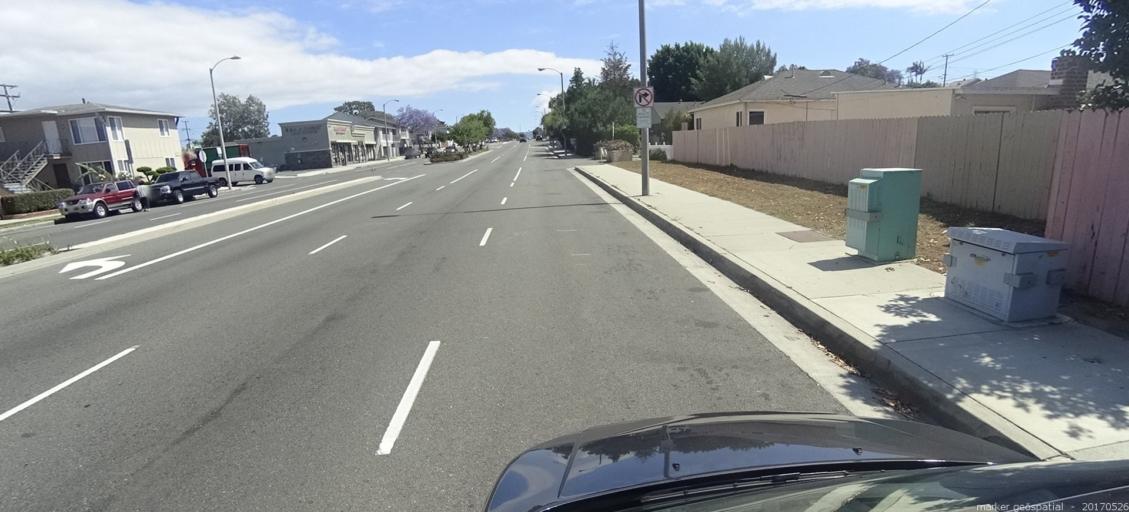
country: US
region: California
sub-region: Los Angeles County
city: Lawndale
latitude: 33.8840
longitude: -118.3614
